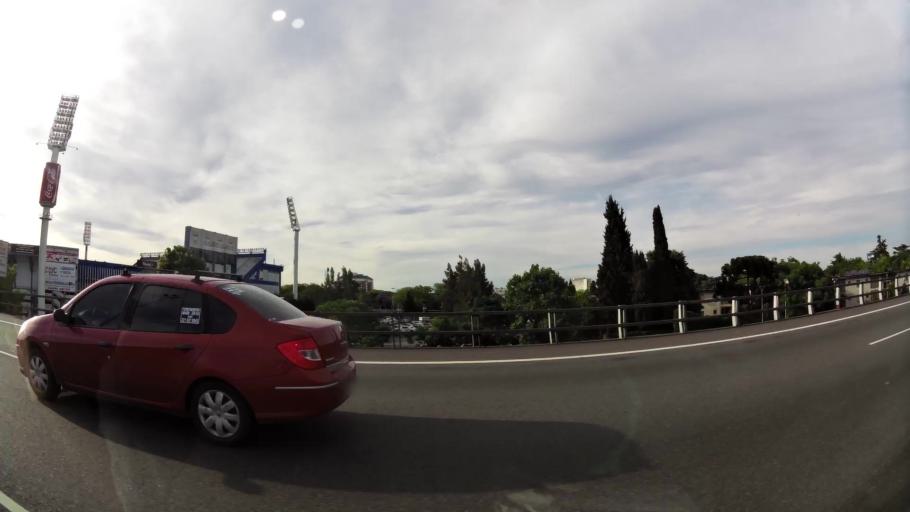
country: AR
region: Buenos Aires F.D.
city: Villa Santa Rita
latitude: -34.6364
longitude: -58.5190
